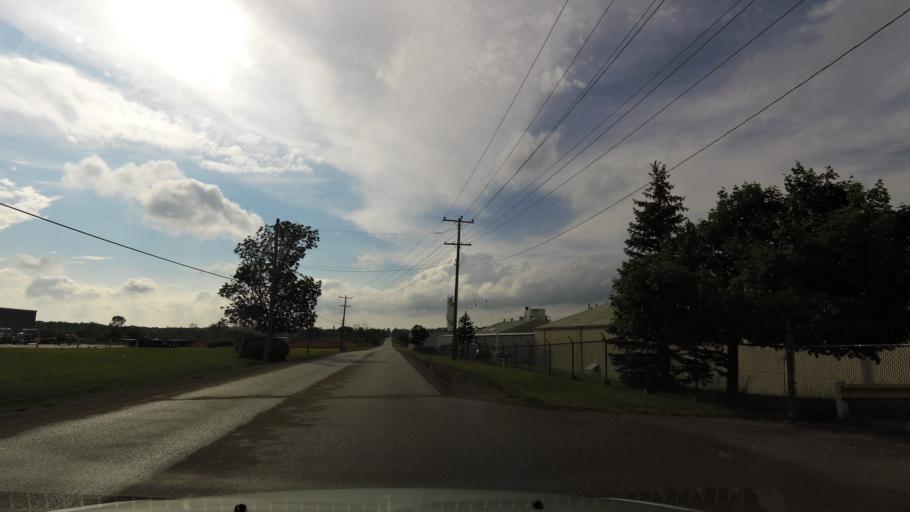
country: CA
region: Ontario
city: Ancaster
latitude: 43.0104
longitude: -80.0155
